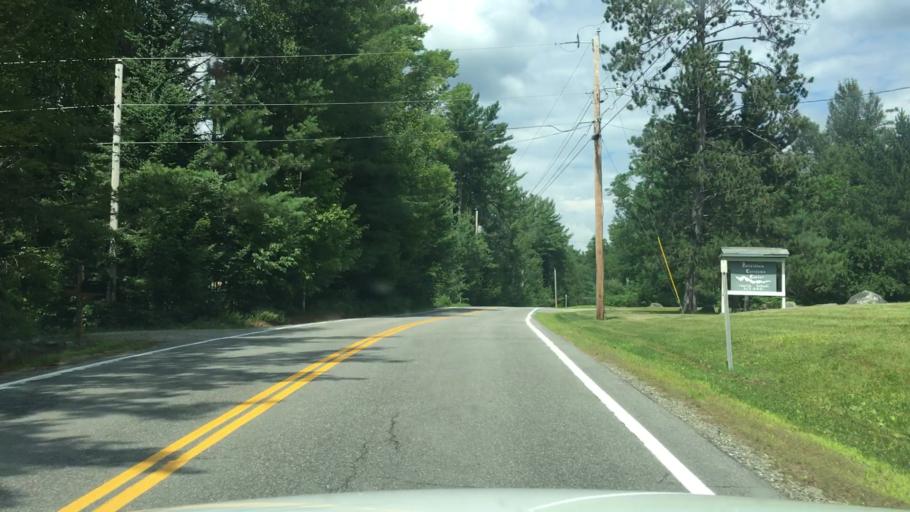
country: US
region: New Hampshire
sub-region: Coos County
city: Whitefield
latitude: 44.3120
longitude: -71.6574
